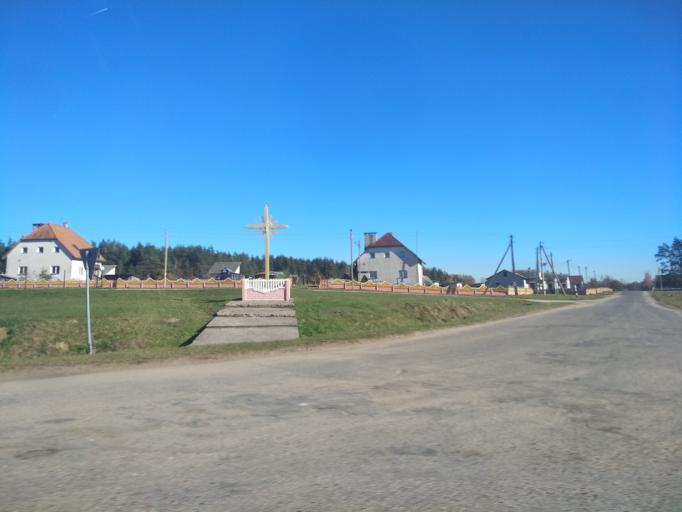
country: BY
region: Minsk
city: Kryvichy
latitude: 54.5707
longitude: 27.2048
